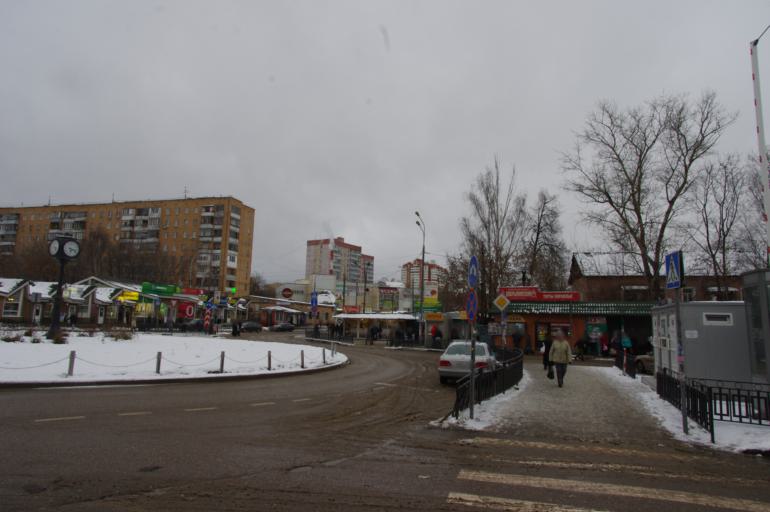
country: RU
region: Moskovskaya
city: Pavshino
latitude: 55.8158
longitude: 37.3416
